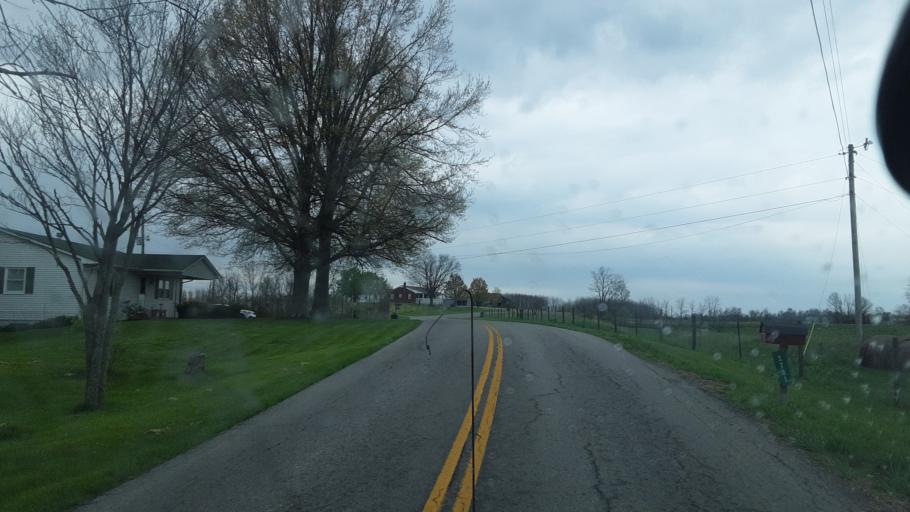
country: US
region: Kentucky
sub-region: Owen County
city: Owenton
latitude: 38.6216
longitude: -84.7862
